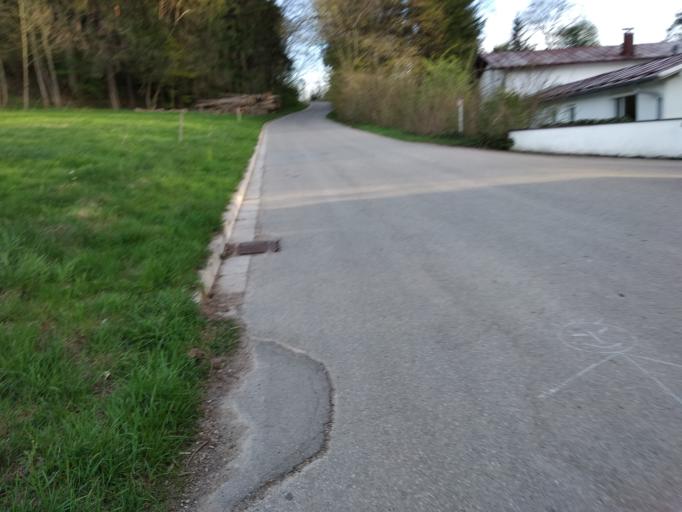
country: DE
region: Bavaria
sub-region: Swabia
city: Lautrach
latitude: 47.8952
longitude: 10.1352
